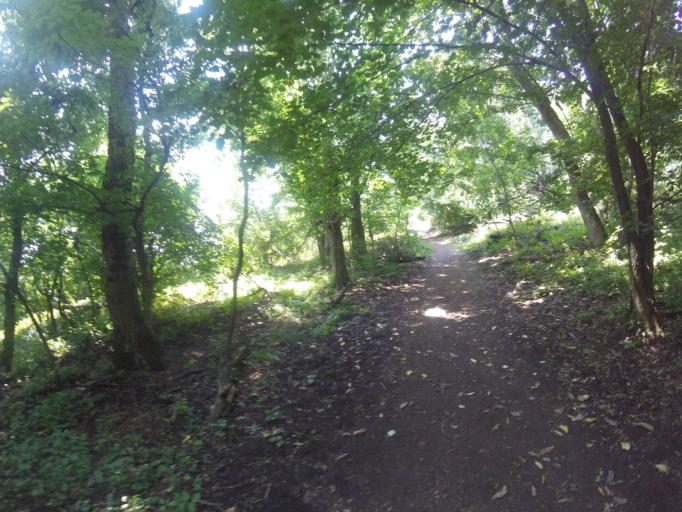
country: HU
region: Veszprem
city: Badacsonytomaj
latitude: 46.7969
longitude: 17.4914
